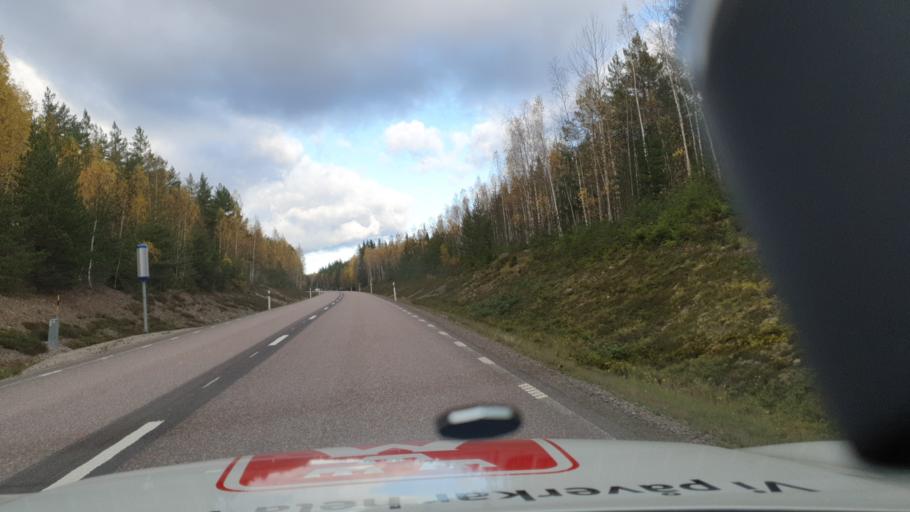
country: SE
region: Gaevleborg
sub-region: Gavle Kommun
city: Hedesunda
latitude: 60.3430
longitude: 16.9477
